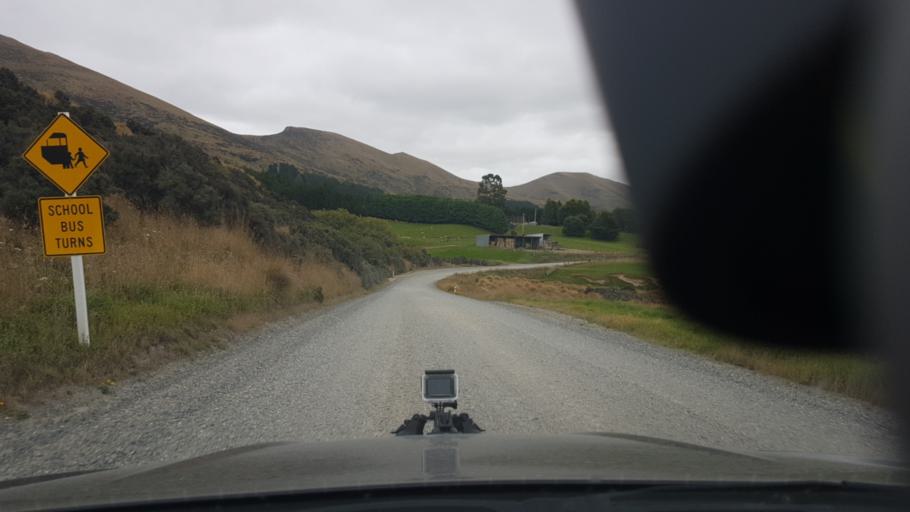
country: NZ
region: Otago
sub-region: Clutha District
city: Papatowai
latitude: -46.3232
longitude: 169.3769
